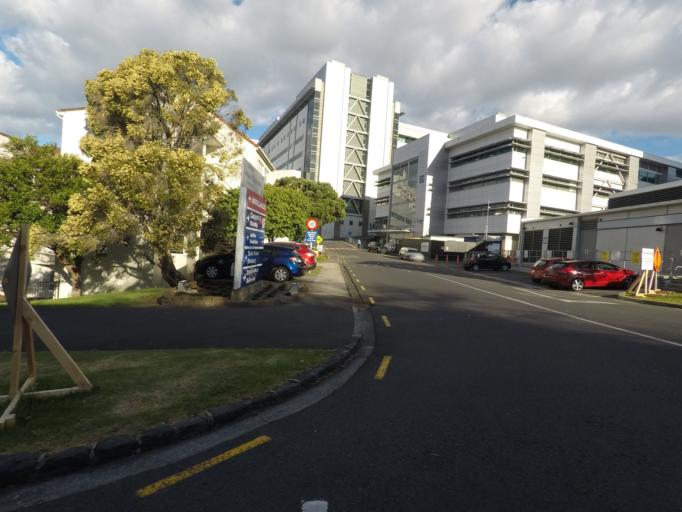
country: NZ
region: Auckland
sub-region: Auckland
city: Auckland
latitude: -36.8595
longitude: 174.7678
